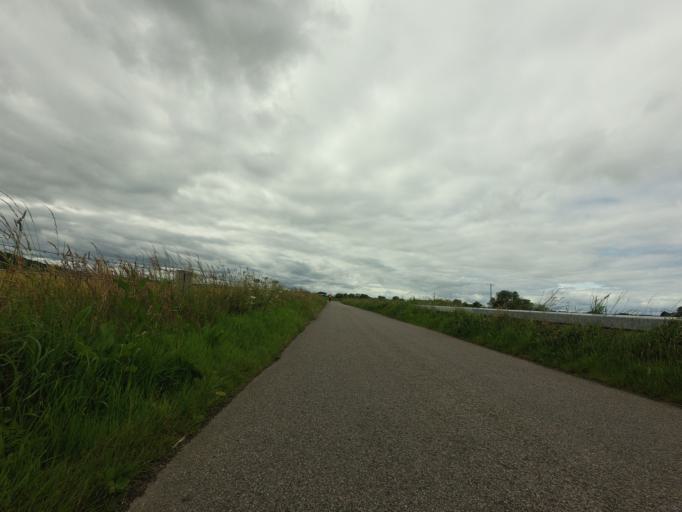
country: GB
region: Scotland
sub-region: Moray
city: Forres
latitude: 57.6286
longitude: -3.6018
